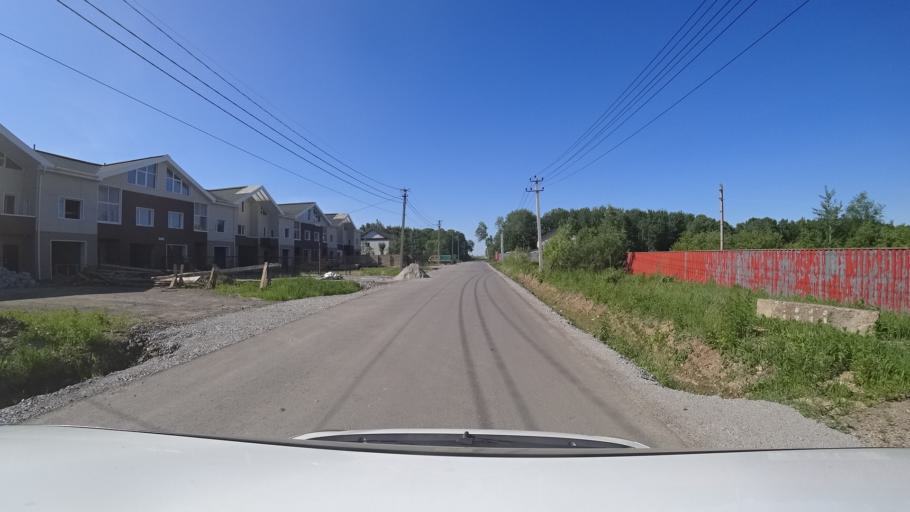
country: RU
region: Khabarovsk Krai
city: Topolevo
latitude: 48.5510
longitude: 135.1744
